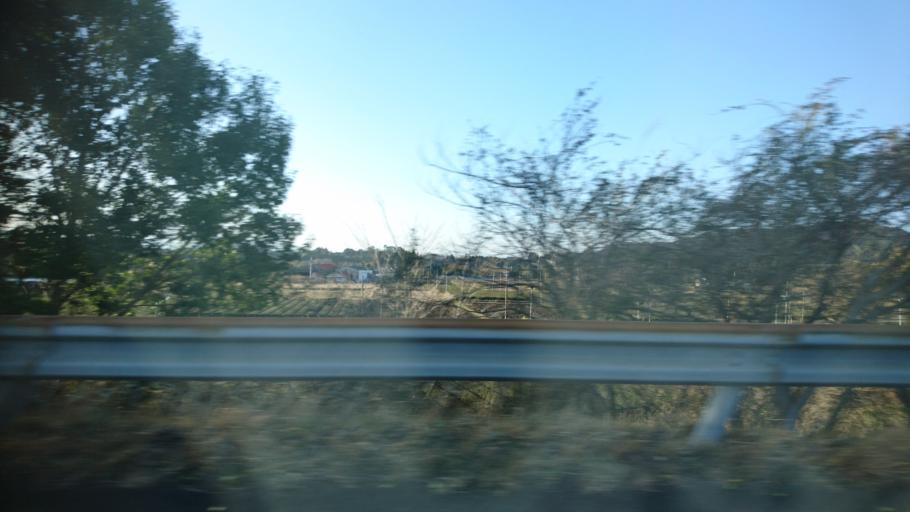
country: JP
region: Miyazaki
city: Miyakonojo
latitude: 31.7924
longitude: 131.1563
